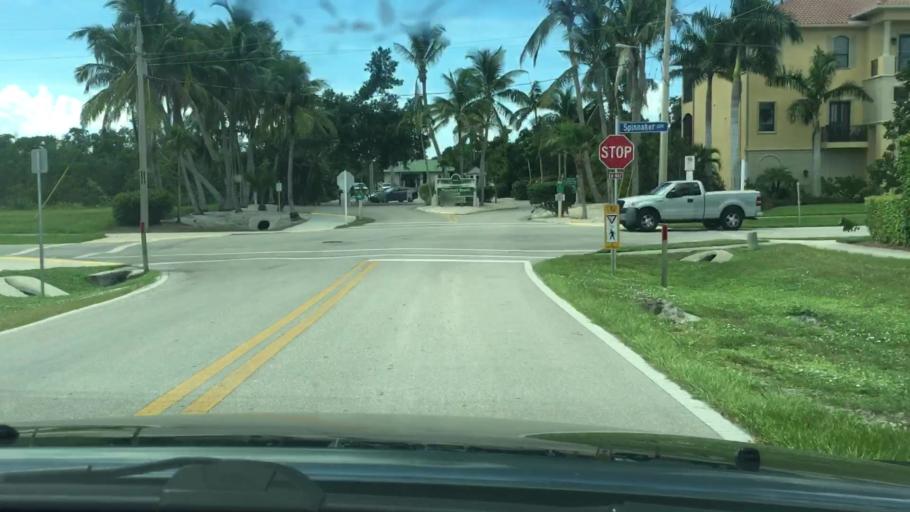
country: US
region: Florida
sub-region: Collier County
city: Marco
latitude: 25.9501
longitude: -81.7421
